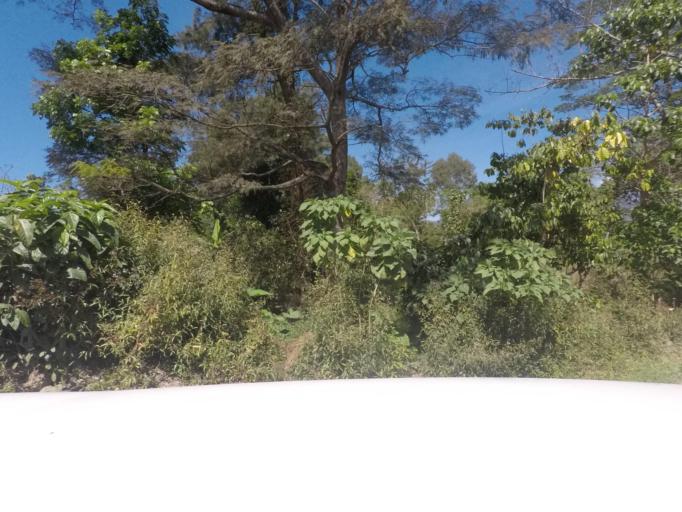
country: TL
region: Ermera
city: Gleno
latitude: -8.7189
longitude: 125.4349
